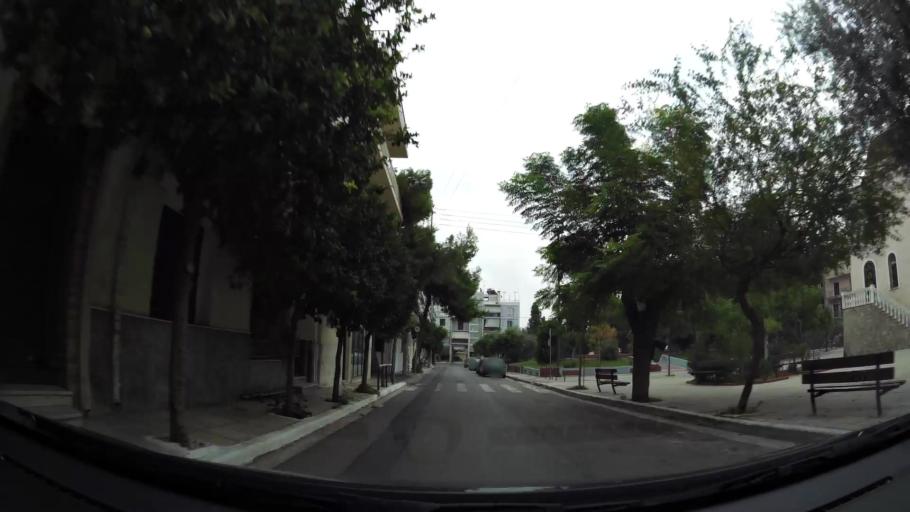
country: GR
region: Attica
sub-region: Nomos Piraios
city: Agios Ioannis Rentis
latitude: 37.9675
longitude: 23.6604
